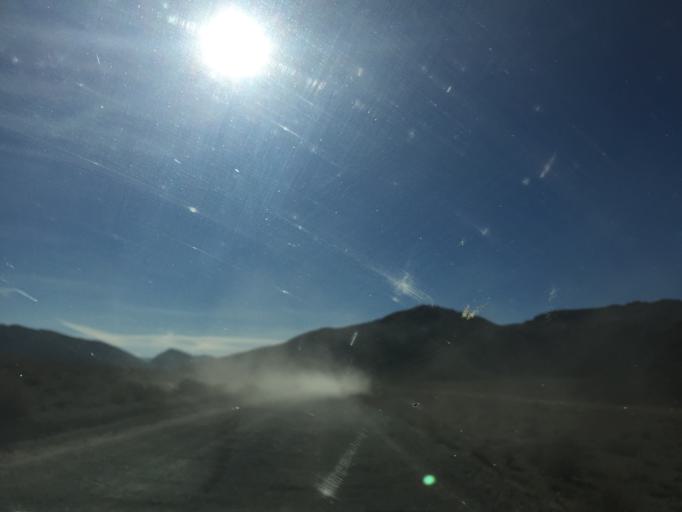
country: US
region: California
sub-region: Inyo County
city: Lone Pine
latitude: 36.8238
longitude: -117.5088
